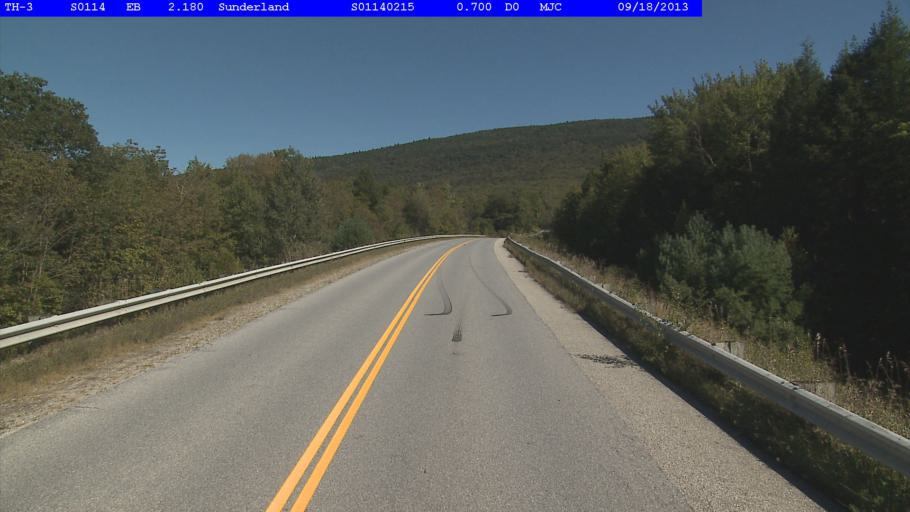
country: US
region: Vermont
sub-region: Bennington County
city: Arlington
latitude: 43.0583
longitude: -73.1250
